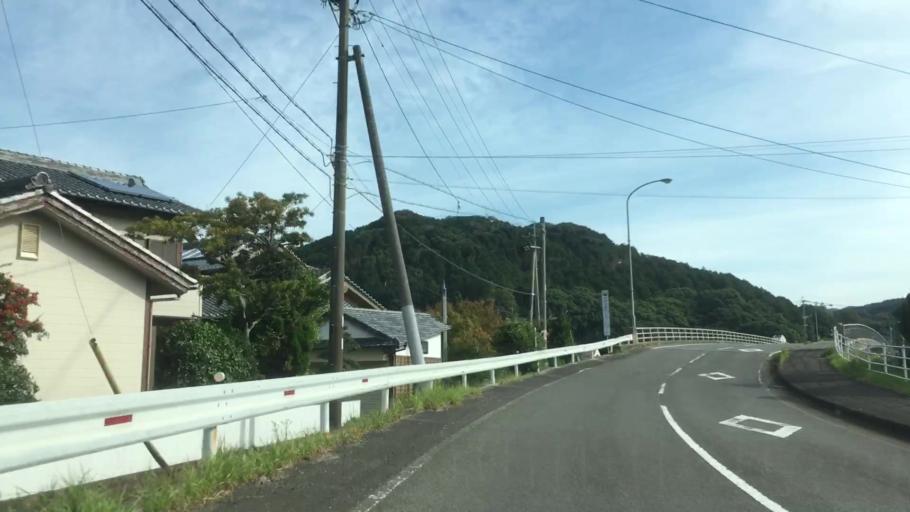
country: JP
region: Nagasaki
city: Sasebo
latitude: 32.9938
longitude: 129.6515
